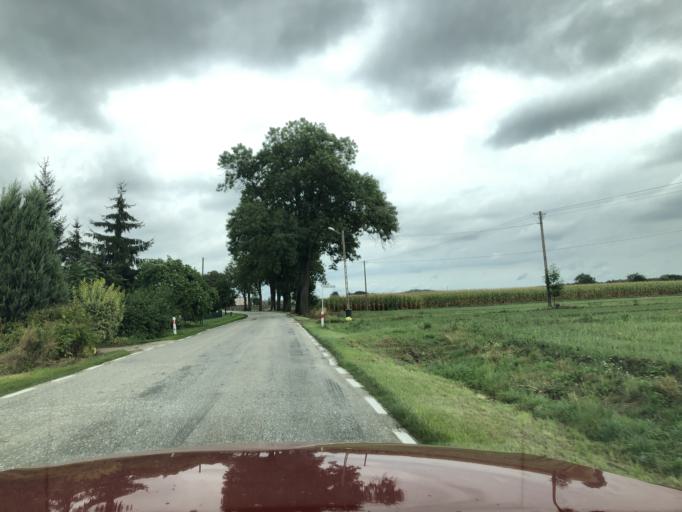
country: PL
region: Greater Poland Voivodeship
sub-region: Powiat szamotulski
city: Wronki
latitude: 52.6158
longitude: 16.3402
